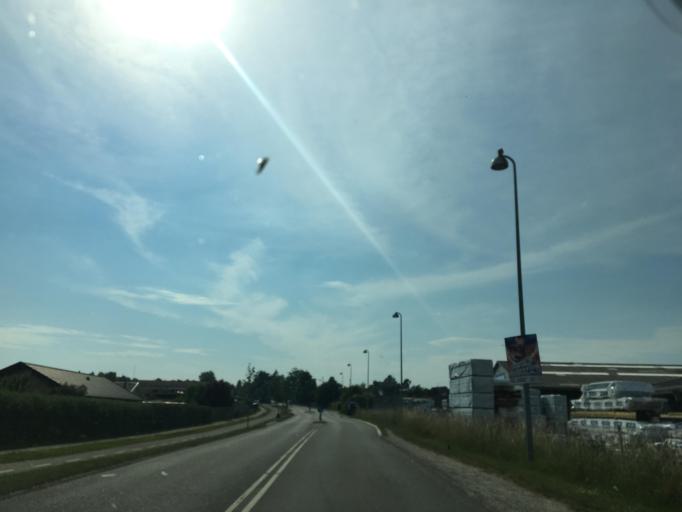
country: DK
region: Zealand
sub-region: Greve Kommune
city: Tune
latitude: 55.5966
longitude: 12.1851
